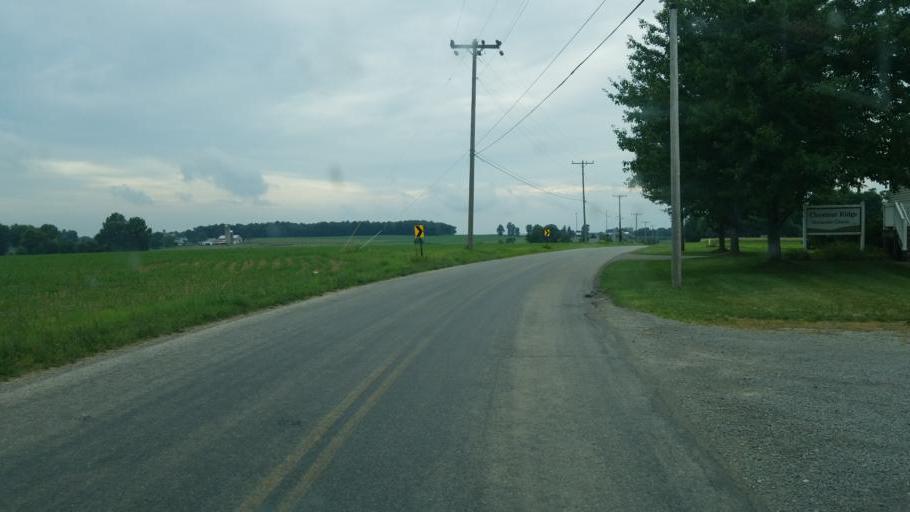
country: US
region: Ohio
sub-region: Wayne County
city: Dalton
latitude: 40.8219
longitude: -81.7253
